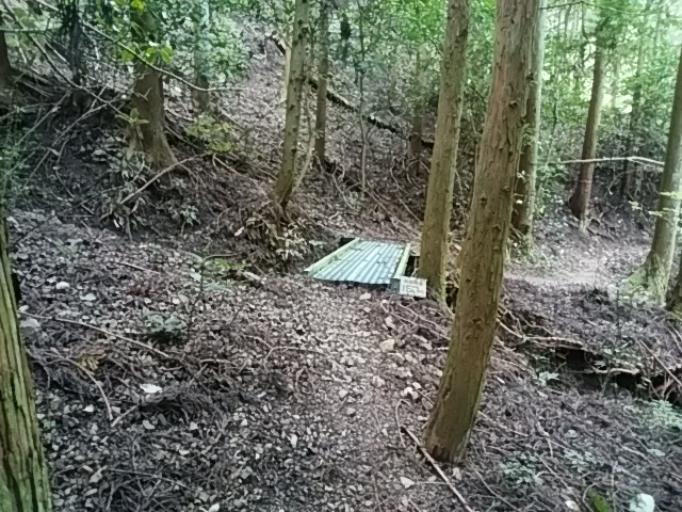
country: JP
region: Shizuoka
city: Kanaya
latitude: 34.8456
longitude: 138.0624
